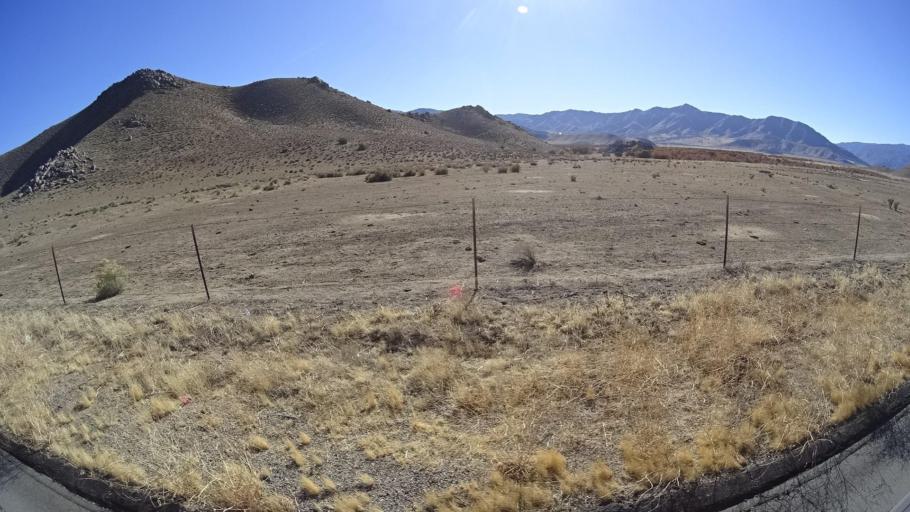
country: US
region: California
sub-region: Kern County
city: Weldon
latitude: 35.6800
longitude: -118.3660
